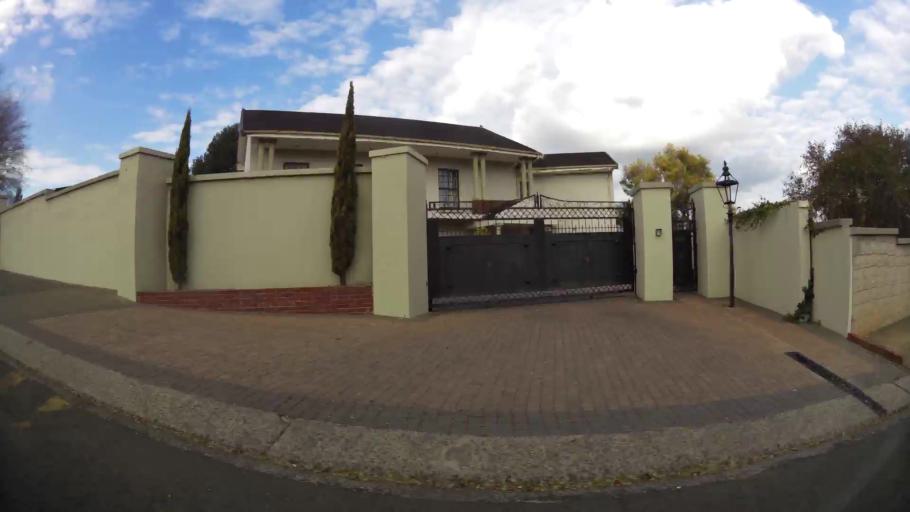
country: ZA
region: Orange Free State
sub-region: Mangaung Metropolitan Municipality
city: Bloemfontein
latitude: -29.0854
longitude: 26.2028
